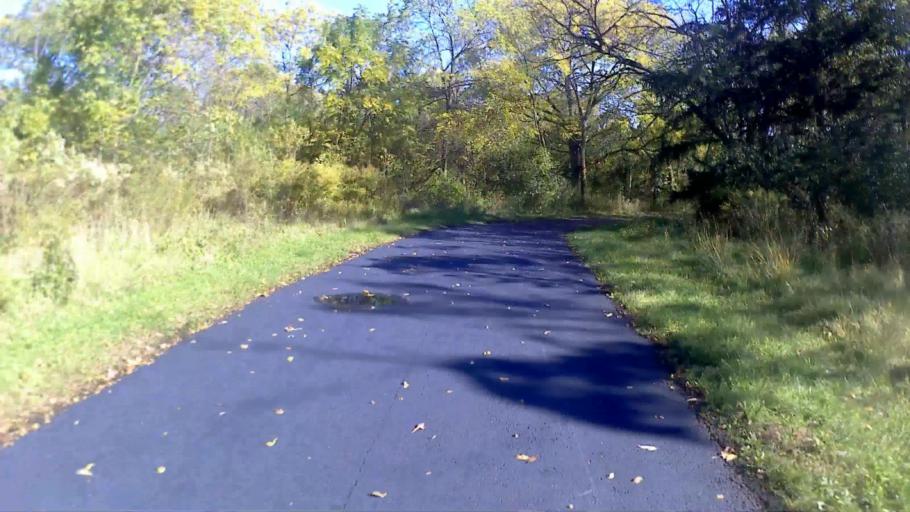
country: US
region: Illinois
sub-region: DuPage County
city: Villa Park
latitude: 41.9092
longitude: -87.9695
